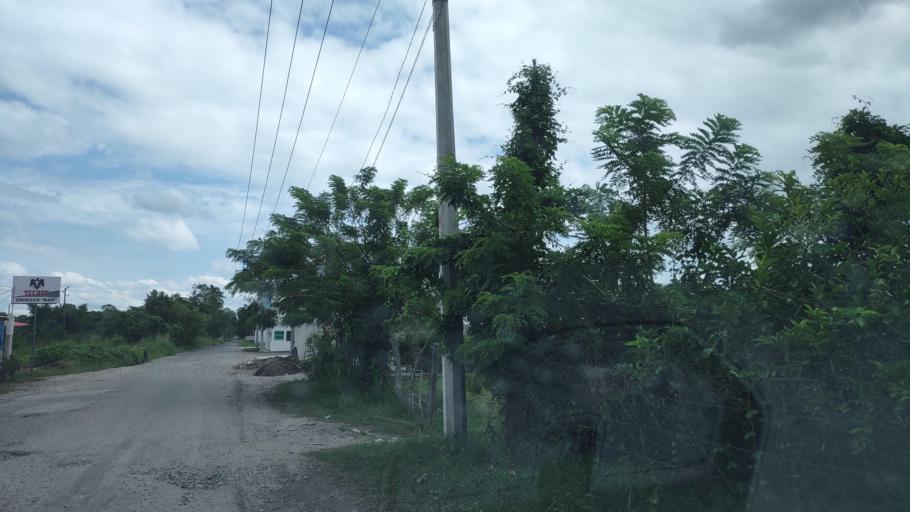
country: MX
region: Veracruz
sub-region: Martinez de la Torre
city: El Progreso
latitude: 20.0971
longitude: -97.0091
